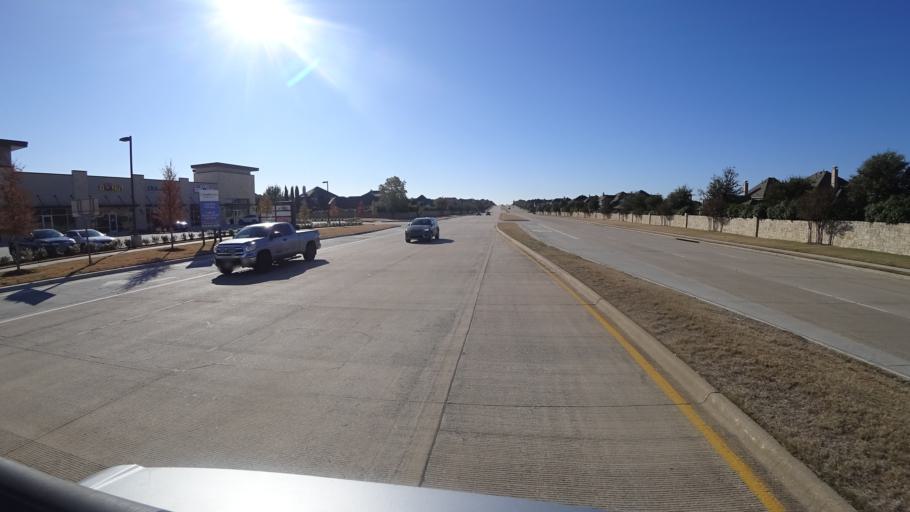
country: US
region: Texas
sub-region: Denton County
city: The Colony
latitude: 33.0454
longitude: -96.9185
